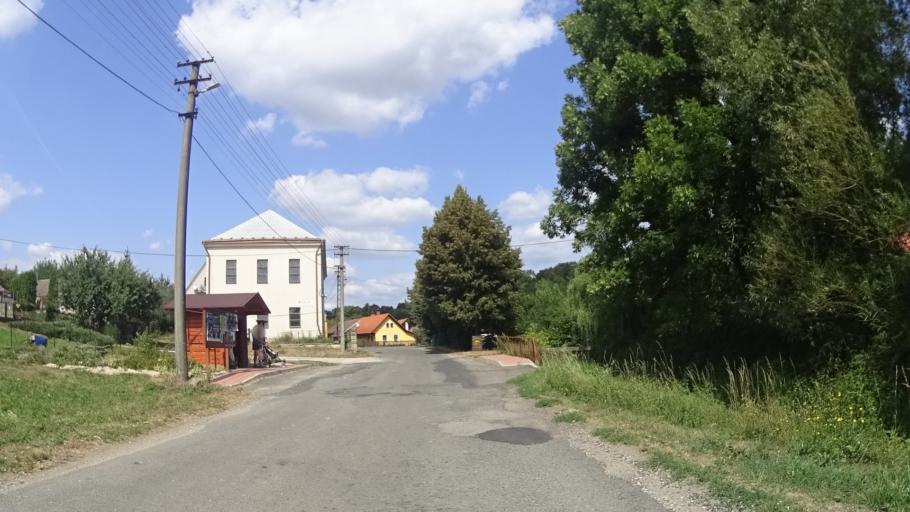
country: CZ
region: Kralovehradecky
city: Kopidlno
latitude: 50.3867
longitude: 15.2964
